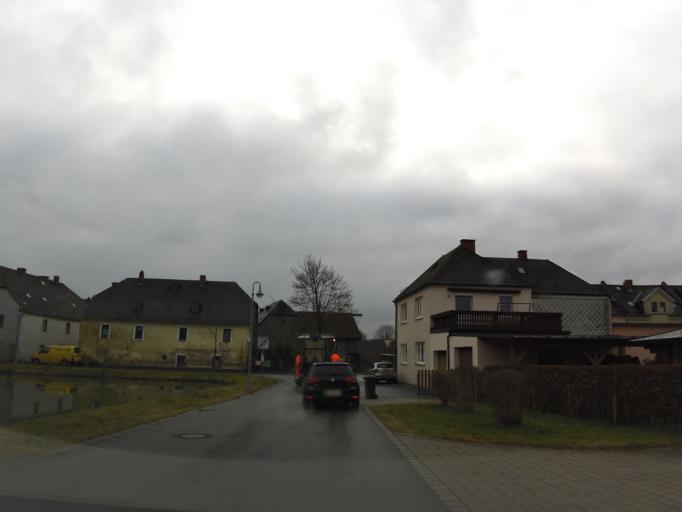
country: DE
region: Bavaria
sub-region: Upper Franconia
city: Wunsiedel
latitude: 50.0448
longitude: 12.0261
